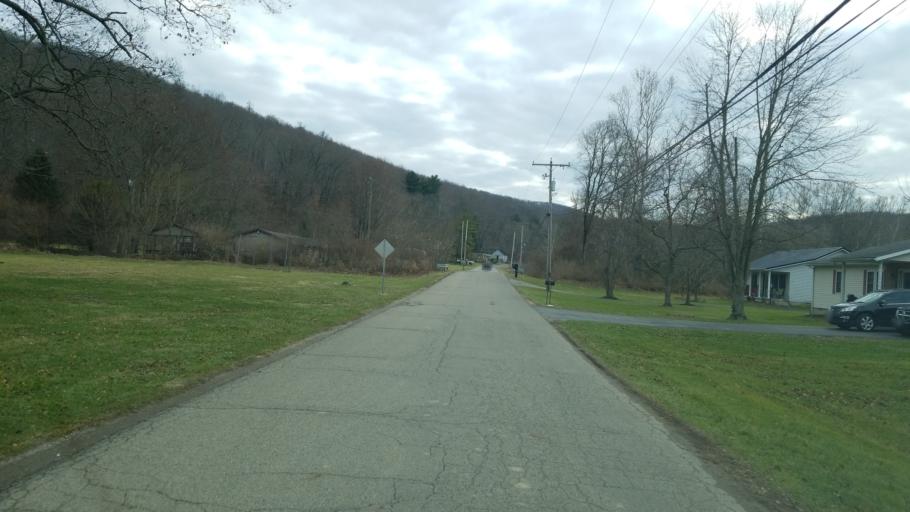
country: US
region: Ohio
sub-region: Highland County
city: Greenfield
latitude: 39.2233
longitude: -83.2693
